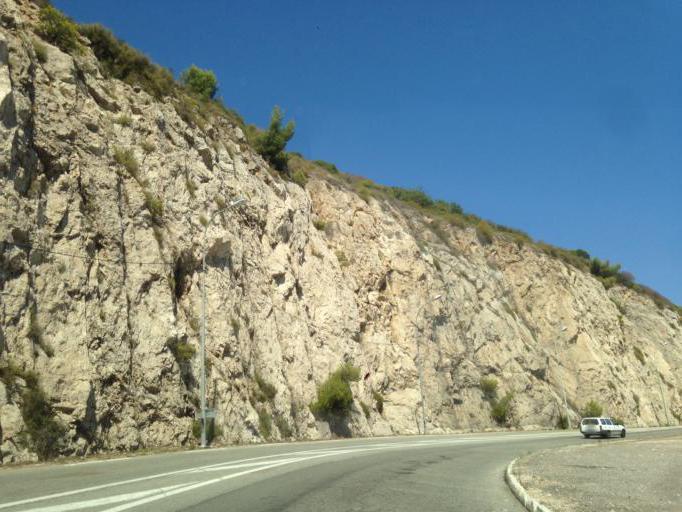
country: FR
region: Provence-Alpes-Cote d'Azur
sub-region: Departement des Alpes-Maritimes
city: Beaulieu-sur-Mer
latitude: 43.7231
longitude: 7.3440
